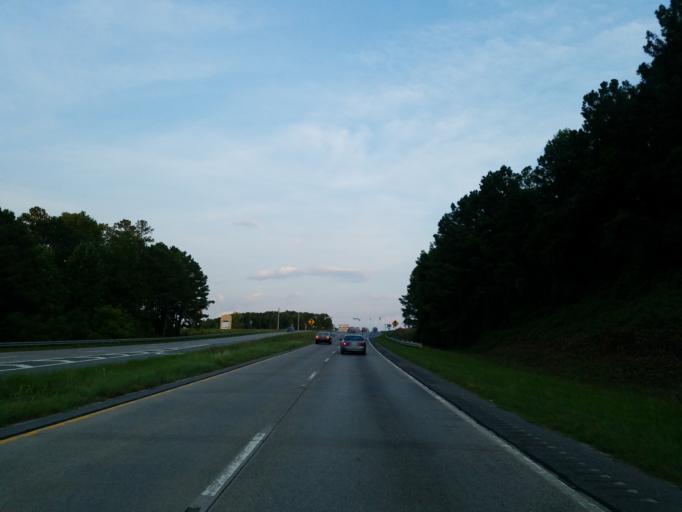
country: US
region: Georgia
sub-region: Pickens County
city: Jasper
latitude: 34.4717
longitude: -84.4625
